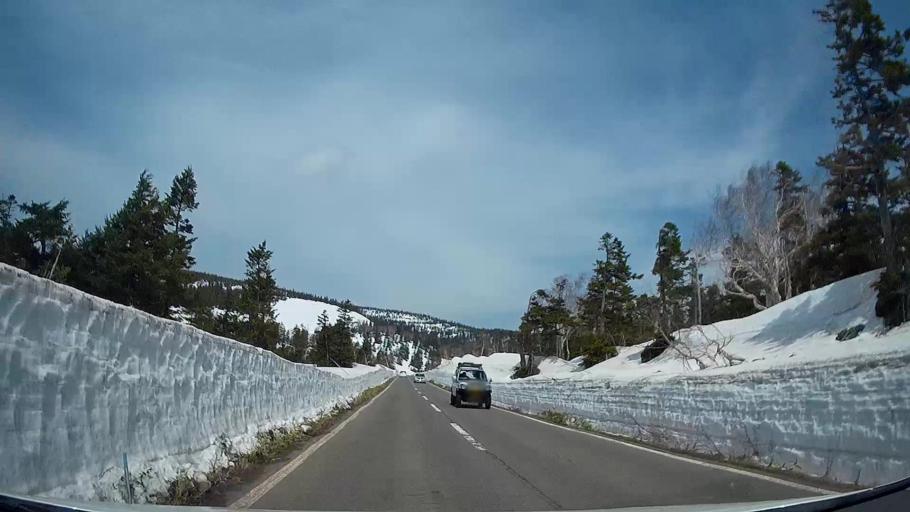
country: JP
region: Akita
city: Hanawa
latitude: 39.9527
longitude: 140.8881
